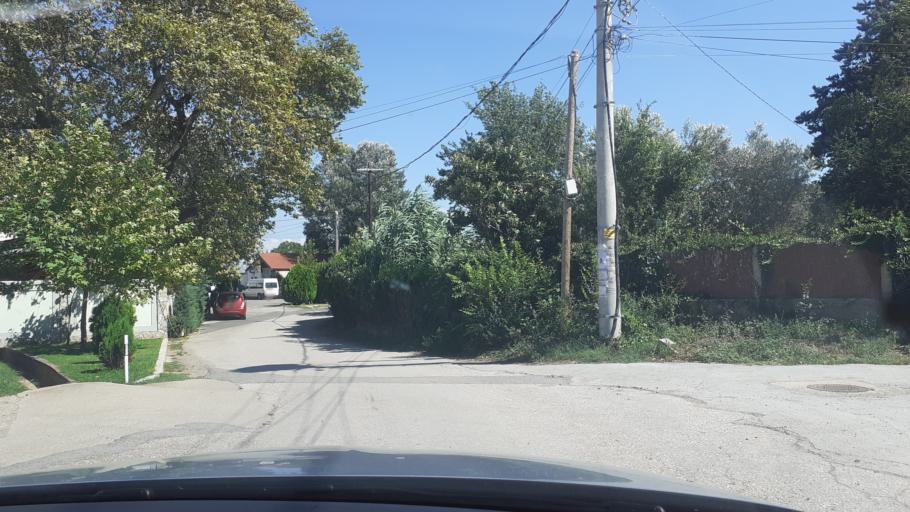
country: MK
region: Gevgelija
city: Gevgelija
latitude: 41.1651
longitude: 22.5039
